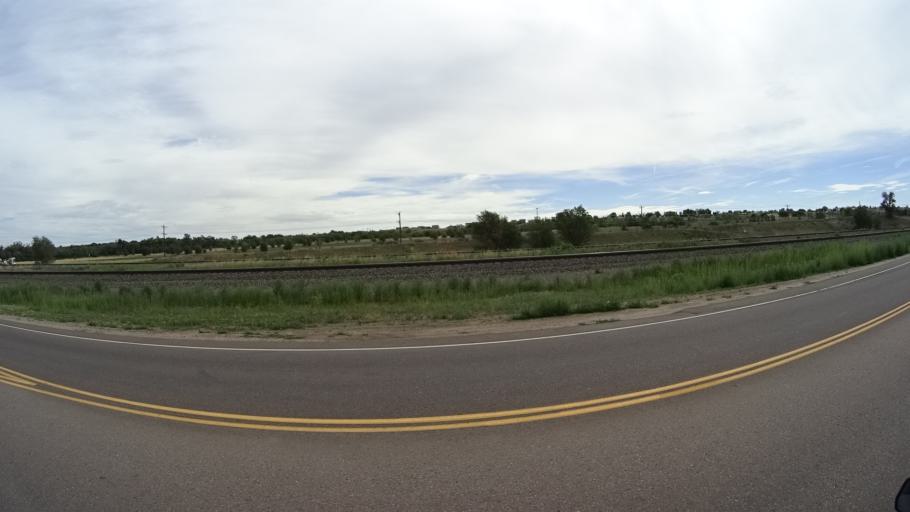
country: US
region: Colorado
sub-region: El Paso County
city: Fountain
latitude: 38.7112
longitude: -104.7126
